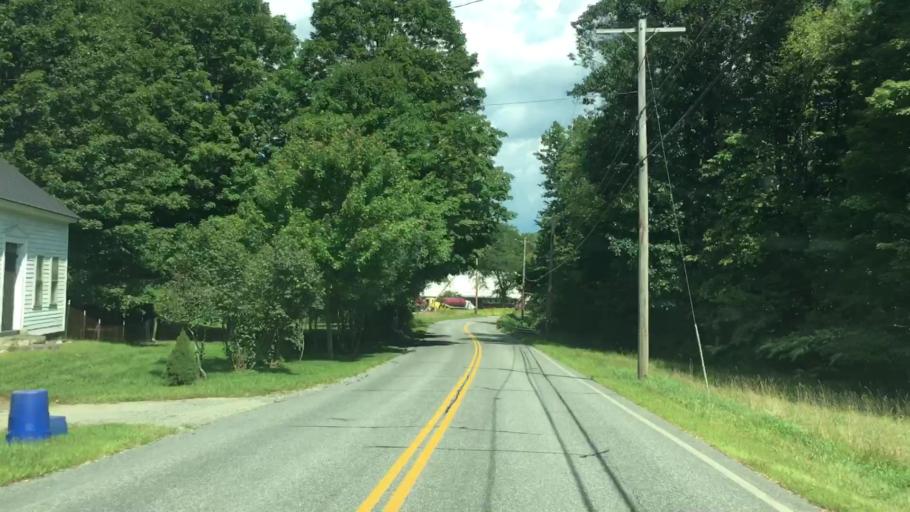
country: US
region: Vermont
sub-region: Windham County
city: Brattleboro
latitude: 42.8125
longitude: -72.5835
